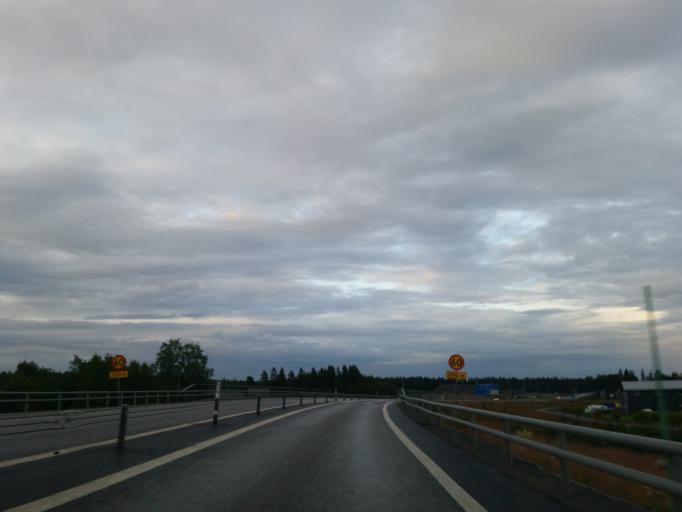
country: SE
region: Vaesterbotten
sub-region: Umea Kommun
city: Roback
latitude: 63.8558
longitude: 20.1980
